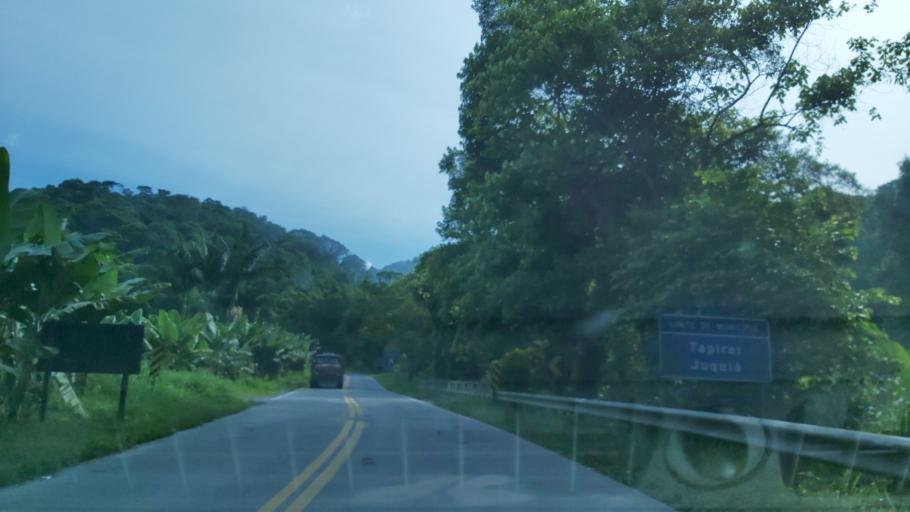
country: BR
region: Sao Paulo
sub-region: Juquia
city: Juquia
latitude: -24.1126
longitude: -47.6261
